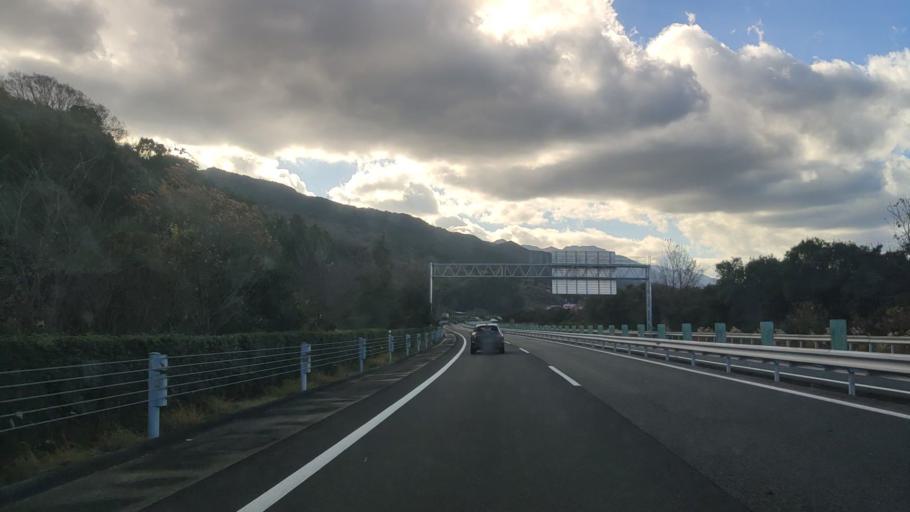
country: JP
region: Ehime
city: Kawanoecho
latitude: 33.9740
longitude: 133.5588
